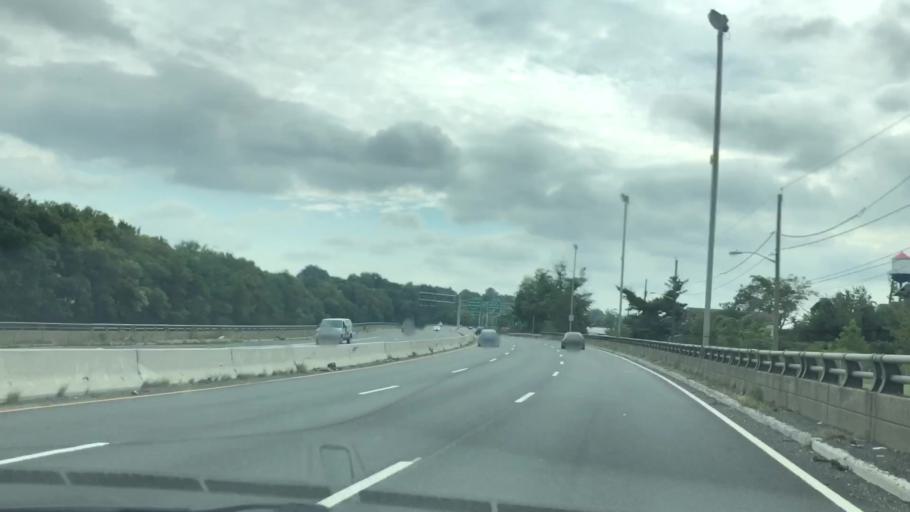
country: US
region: New Jersey
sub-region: Essex County
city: Belleville
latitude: 40.7845
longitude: -74.1494
